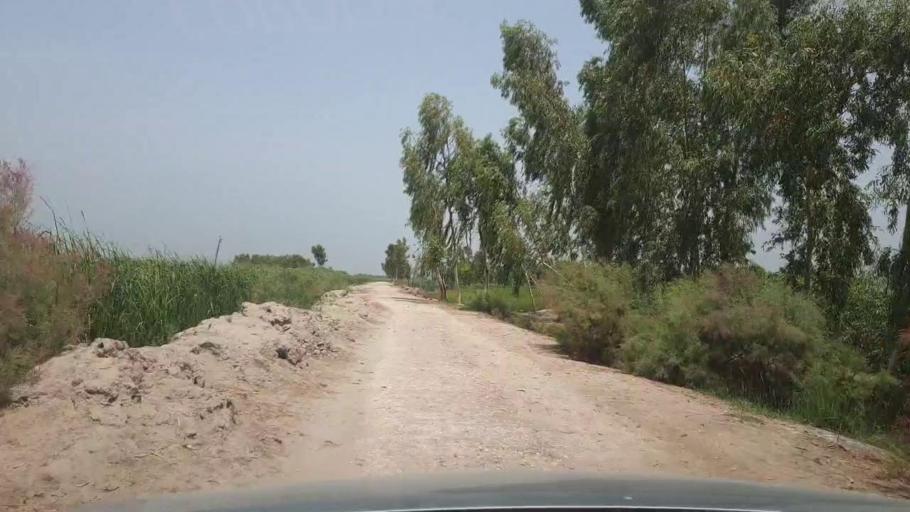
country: PK
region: Sindh
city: Garhi Yasin
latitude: 27.9202
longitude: 68.4325
